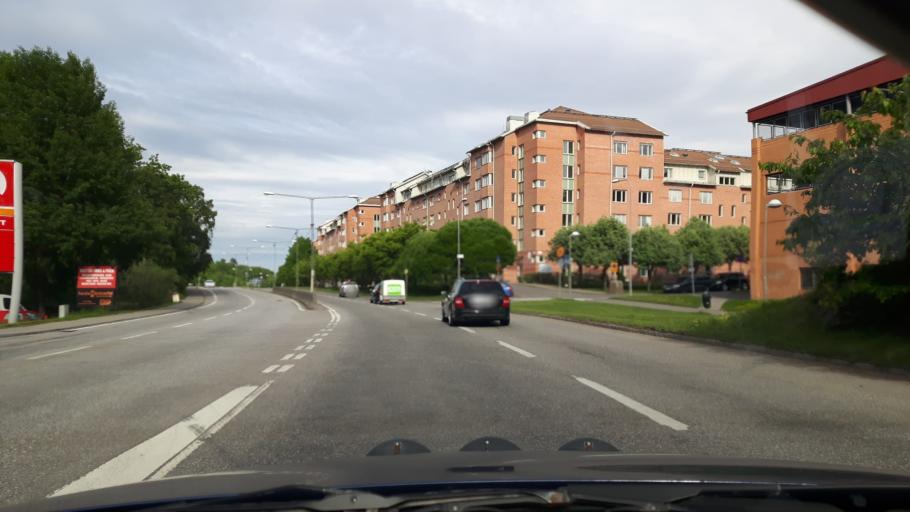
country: SE
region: Stockholm
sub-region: Stockholms Kommun
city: Arsta
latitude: 59.2355
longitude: 18.0971
